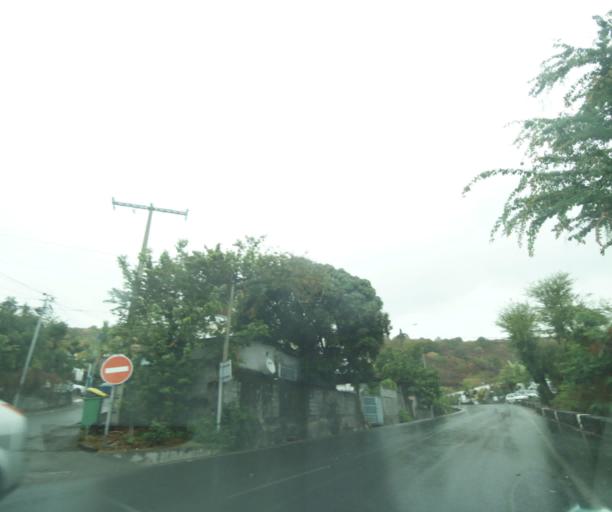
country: RE
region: Reunion
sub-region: Reunion
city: Saint-Paul
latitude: -21.0138
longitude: 55.2772
